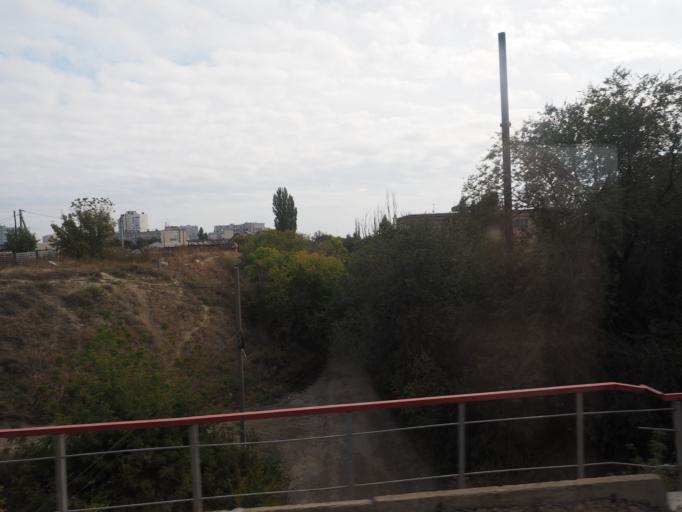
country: RU
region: Volgograd
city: Volgograd
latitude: 48.6839
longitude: 44.4700
